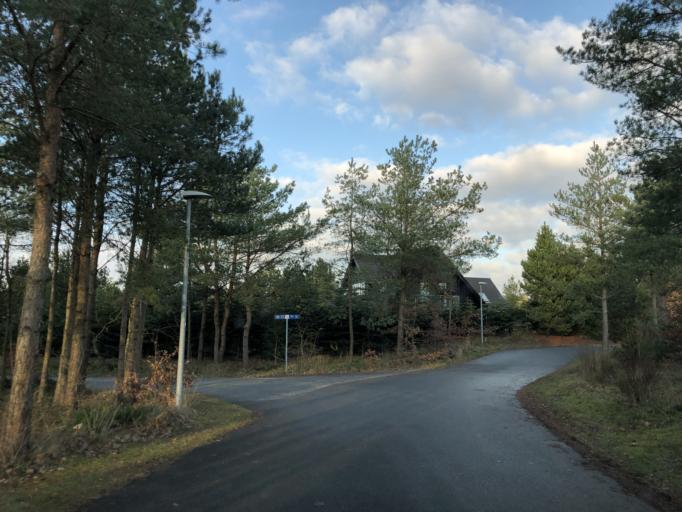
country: DK
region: Central Jutland
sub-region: Holstebro Kommune
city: Ulfborg
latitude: 56.3192
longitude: 8.4370
